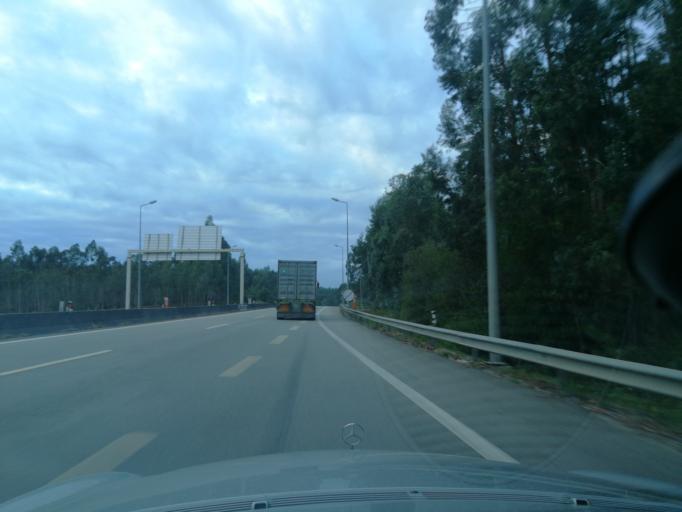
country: PT
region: Aveiro
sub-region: Albergaria-A-Velha
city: Albergaria-a-Velha
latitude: 40.6759
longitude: -8.4768
